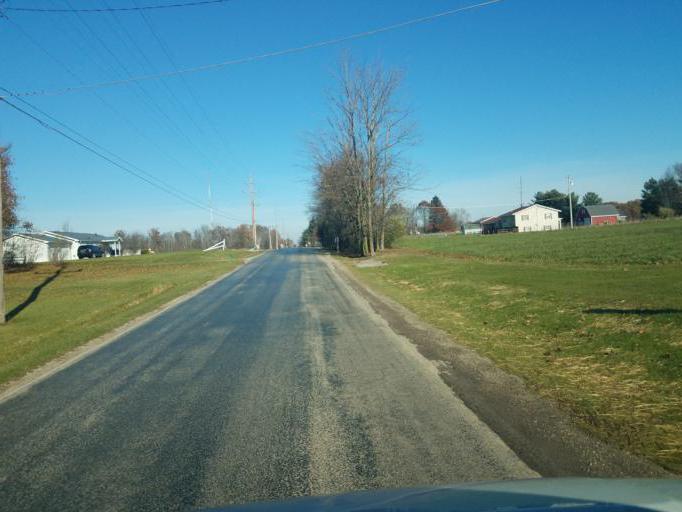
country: US
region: Ohio
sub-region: Ashland County
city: Ashland
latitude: 40.8271
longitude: -82.3493
